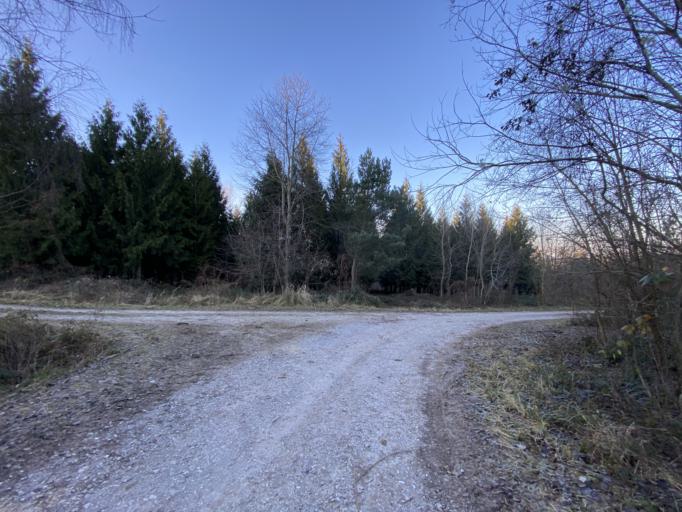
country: AT
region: Lower Austria
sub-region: Politischer Bezirk Sankt Polten
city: Boheimkirchen
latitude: 48.2147
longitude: 15.7134
